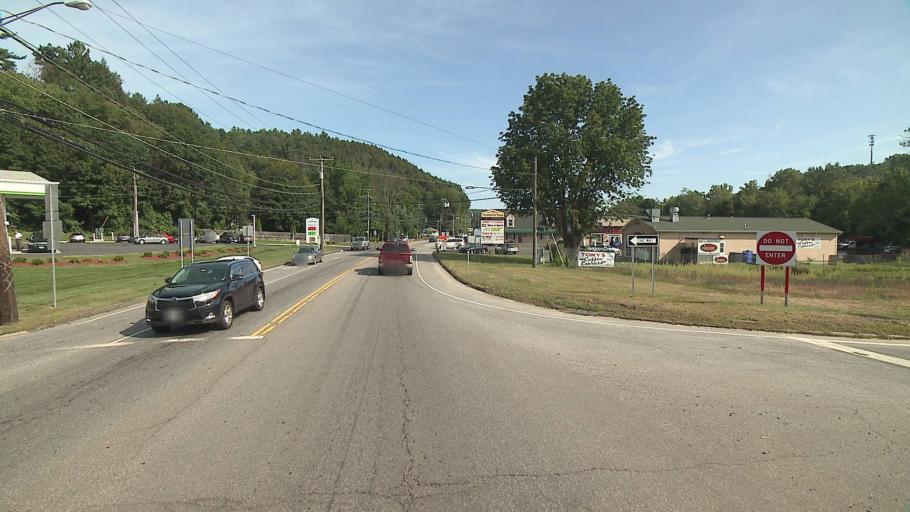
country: US
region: Connecticut
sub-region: Litchfield County
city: Thomaston
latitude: 41.6597
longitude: -73.0803
